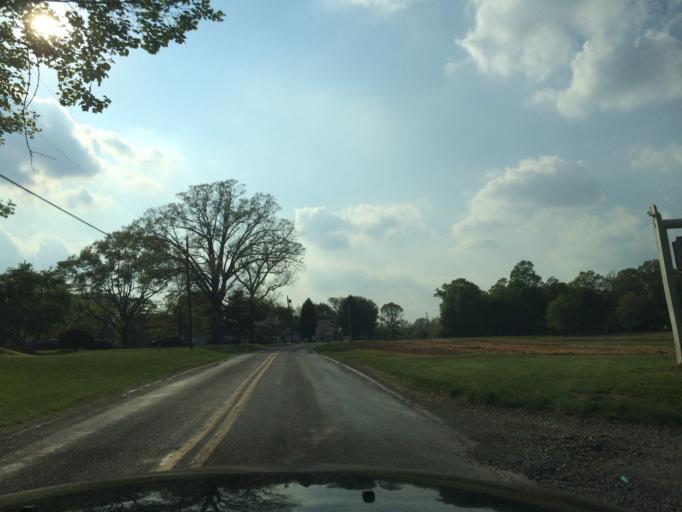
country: US
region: Maryland
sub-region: Carroll County
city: Mount Airy
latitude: 39.3011
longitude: -77.0958
